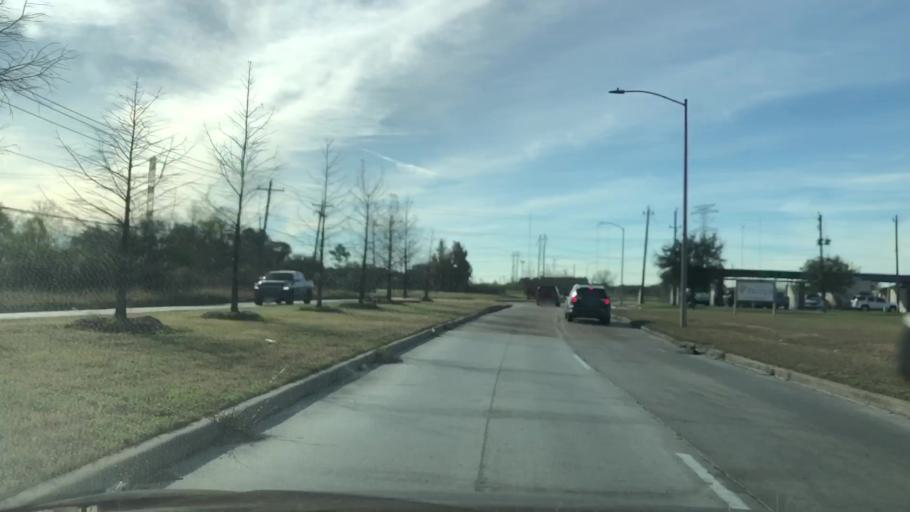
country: US
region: Texas
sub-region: Fort Bend County
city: Missouri City
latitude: 29.6326
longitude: -95.4933
